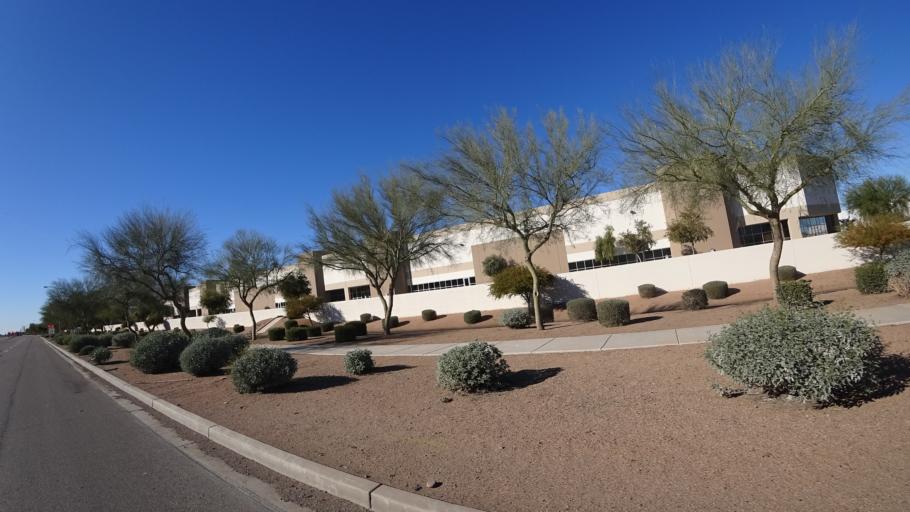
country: US
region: Arizona
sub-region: Maricopa County
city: Tolleson
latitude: 33.4369
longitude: -112.2421
